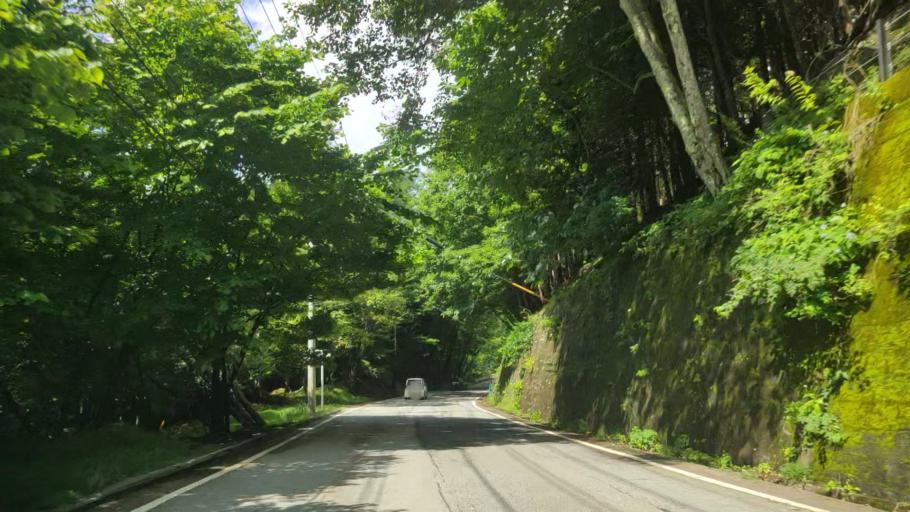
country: JP
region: Yamanashi
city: Enzan
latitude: 35.8355
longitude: 138.7658
